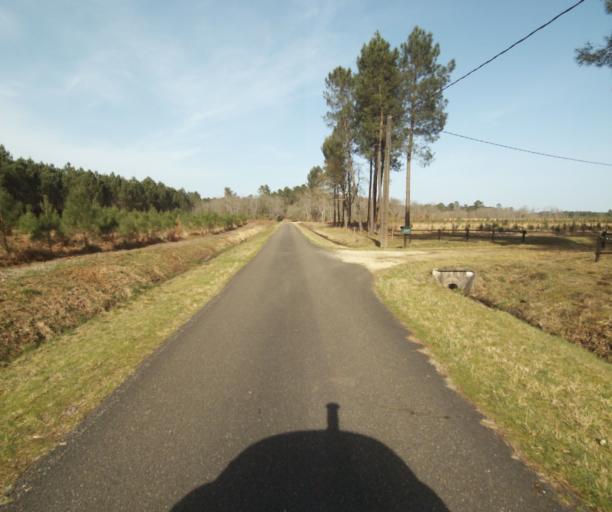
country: FR
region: Aquitaine
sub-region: Departement des Landes
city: Sarbazan
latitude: 44.1216
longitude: -0.1607
